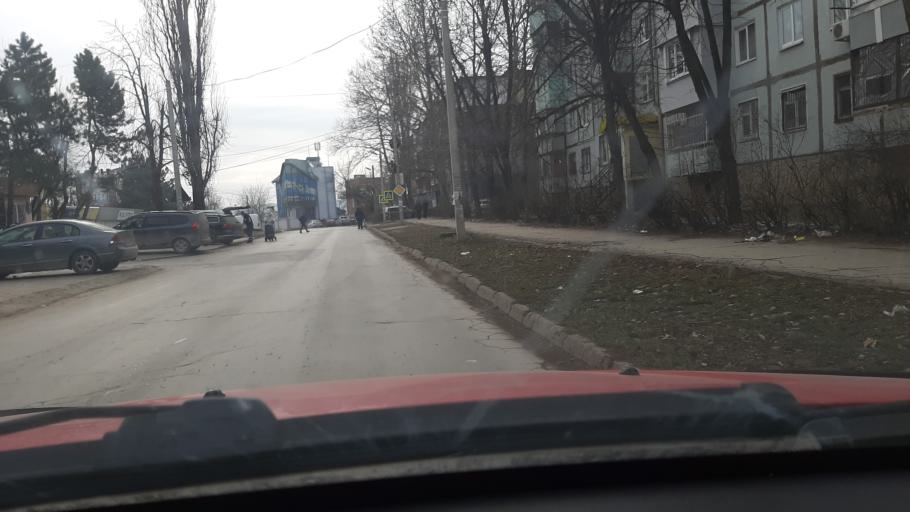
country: MD
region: Chisinau
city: Vatra
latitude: 47.0303
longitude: 28.7800
